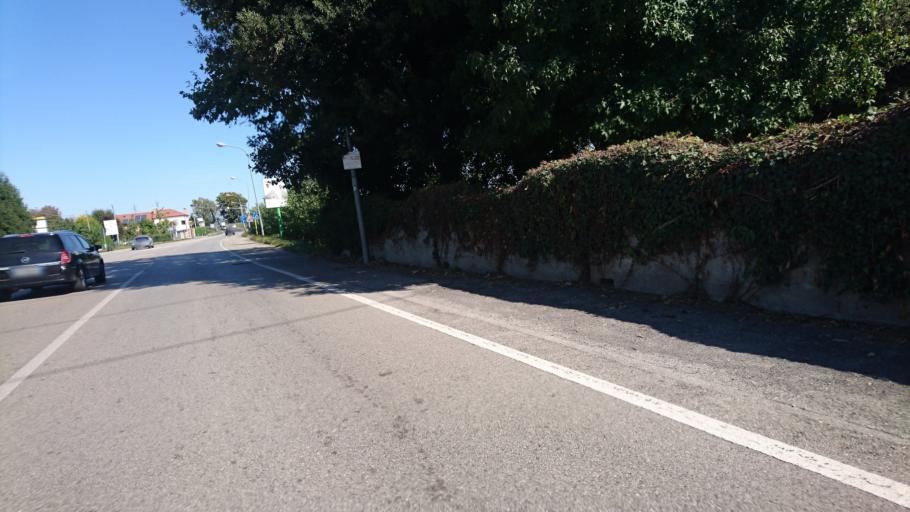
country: IT
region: Veneto
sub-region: Provincia di Venezia
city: Fosso
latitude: 45.3980
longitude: 12.0515
